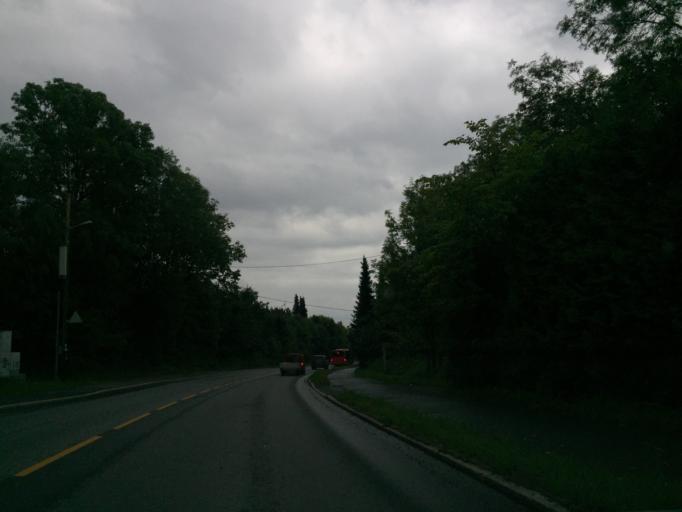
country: NO
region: Oslo
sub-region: Oslo
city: Sjolyststranda
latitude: 59.9443
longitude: 10.6803
